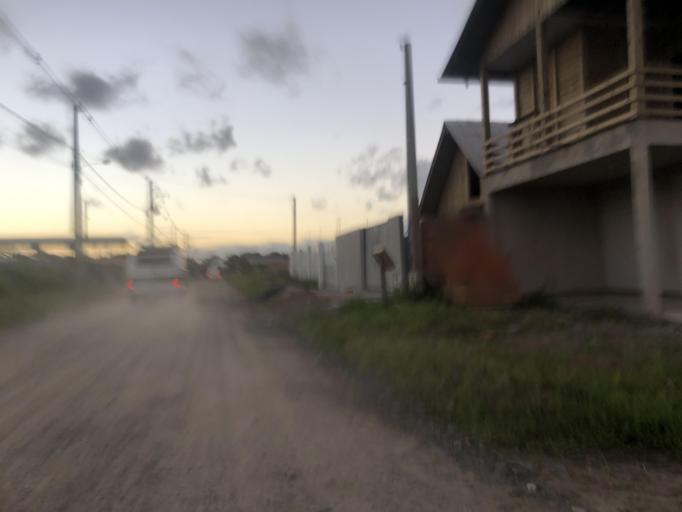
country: BR
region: Santa Catarina
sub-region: Sao Francisco Do Sul
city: Sao Francisco do Sul
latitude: -26.2216
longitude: -48.5305
